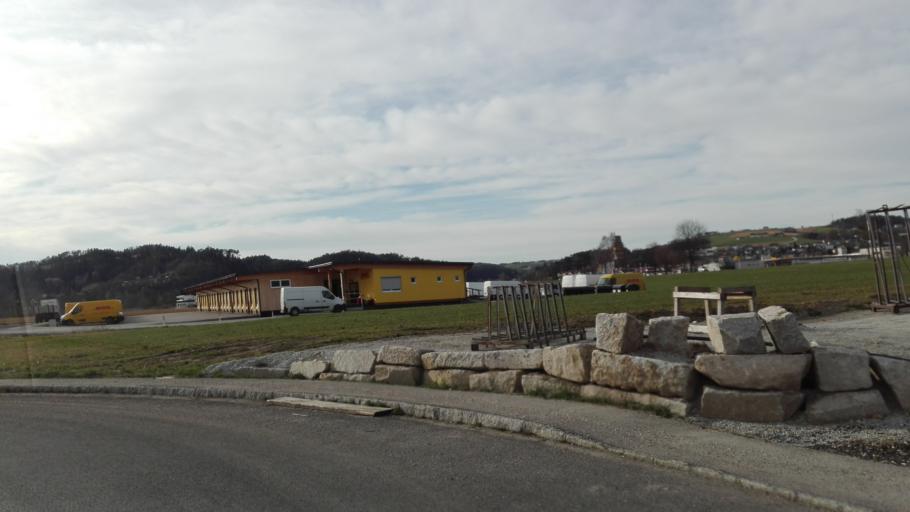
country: AT
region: Upper Austria
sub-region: Politischer Bezirk Urfahr-Umgebung
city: Walding
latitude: 48.3415
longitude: 14.1641
